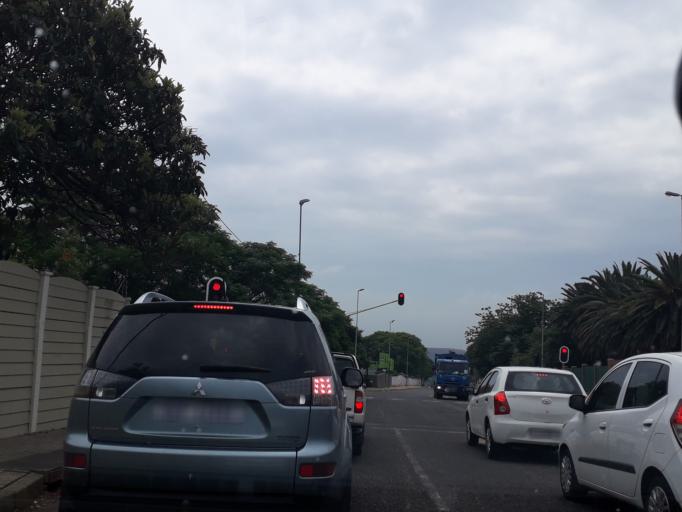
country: ZA
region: Gauteng
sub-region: City of Johannesburg Metropolitan Municipality
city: Johannesburg
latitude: -26.1075
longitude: 27.9840
